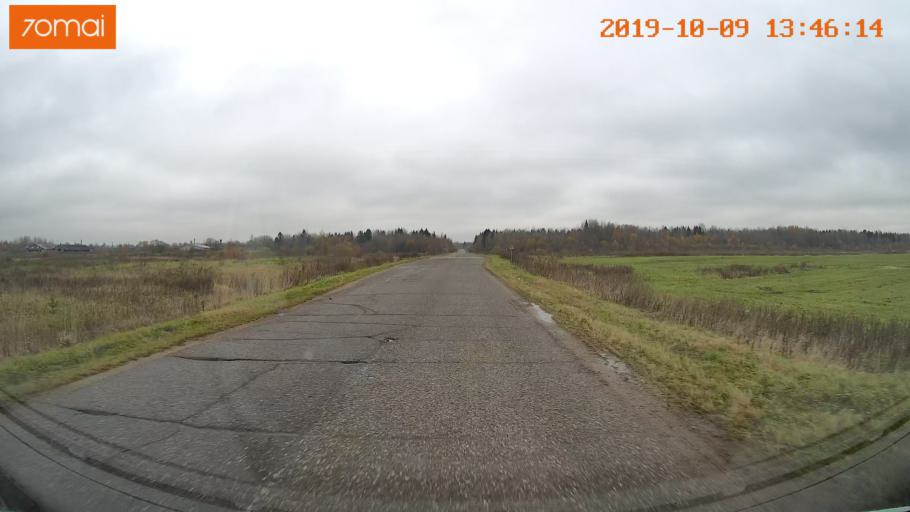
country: RU
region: Kostroma
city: Buy
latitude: 58.3818
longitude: 41.2164
